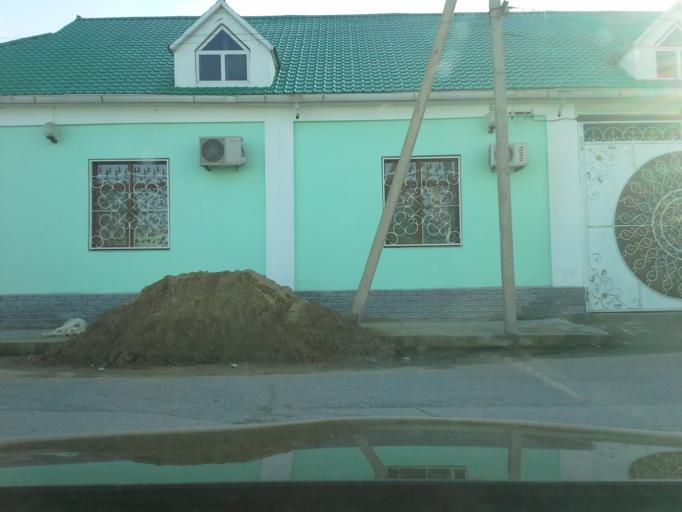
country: TM
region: Ahal
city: Abadan
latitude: 38.0292
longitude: 58.2261
